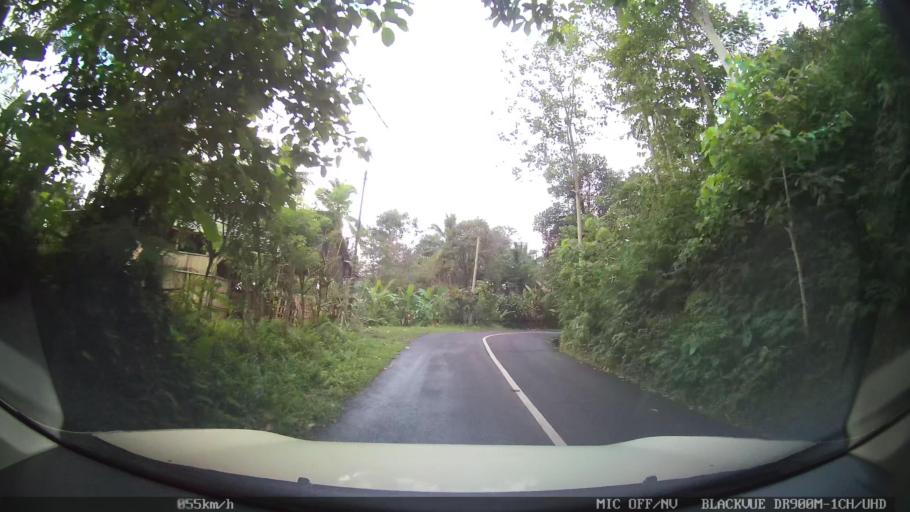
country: ID
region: Bali
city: Peneng
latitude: -8.3651
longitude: 115.1792
